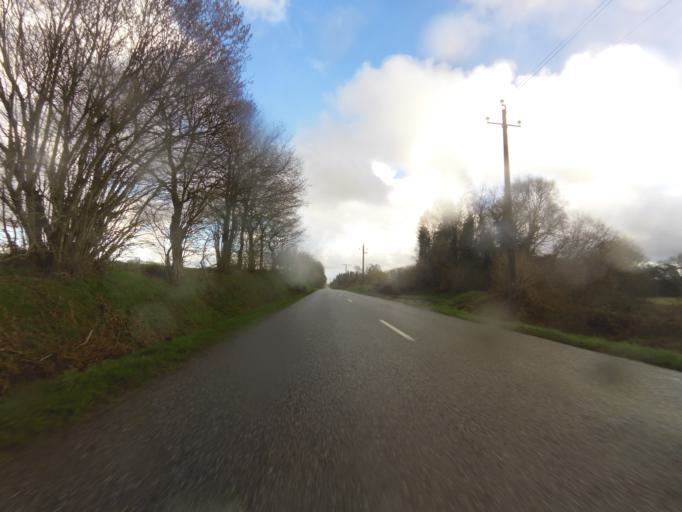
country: FR
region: Brittany
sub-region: Departement du Morbihan
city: Langonnet
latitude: 48.1440
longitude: -3.4796
